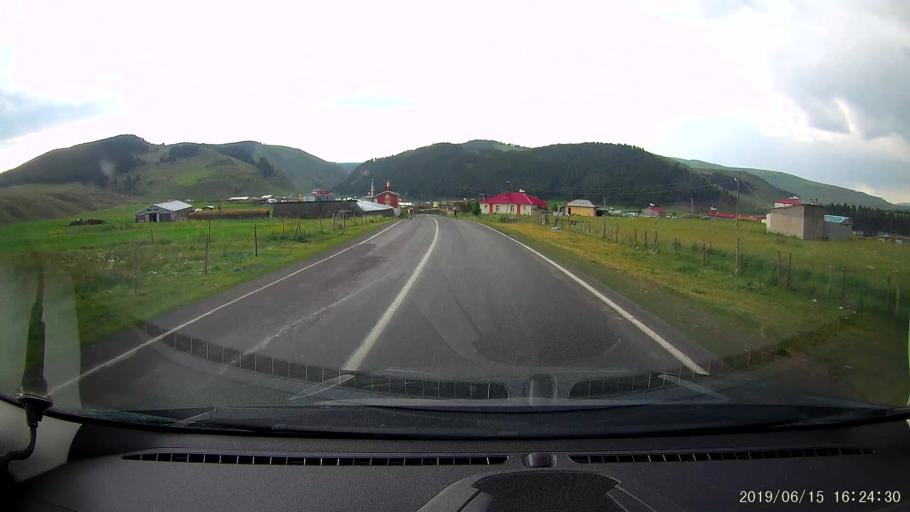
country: TR
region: Ardahan
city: Hanak
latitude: 41.1640
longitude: 42.8708
